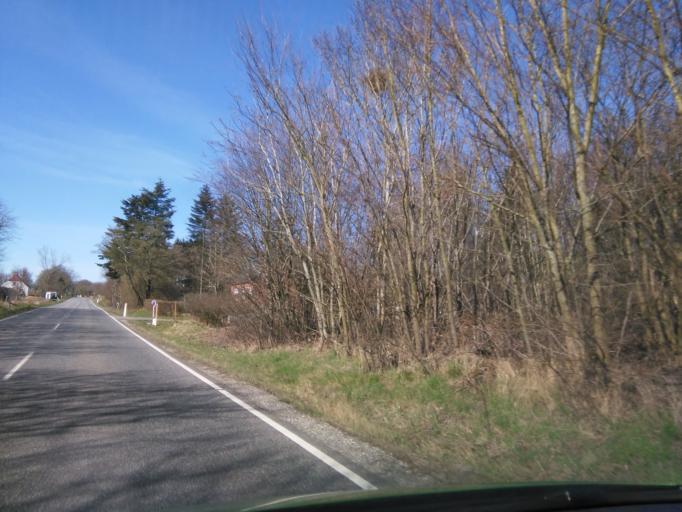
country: DK
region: Central Jutland
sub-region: Skanderborg Kommune
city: Ry
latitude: 56.0233
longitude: 9.8006
